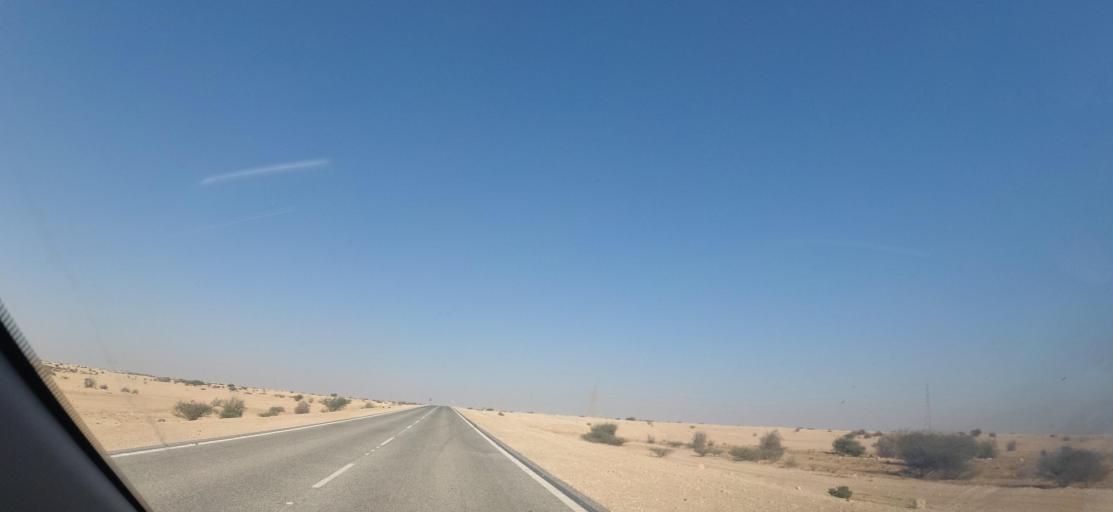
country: QA
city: Al Jumayliyah
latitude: 25.6299
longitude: 51.0948
